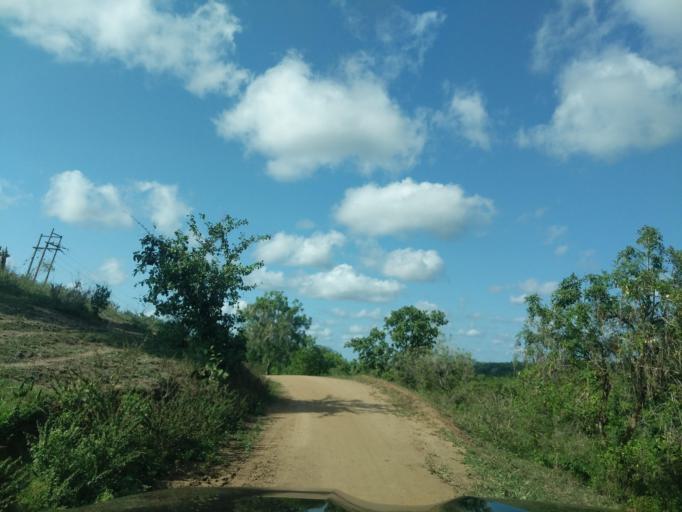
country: TZ
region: Tanga
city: Muheza
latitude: -5.4191
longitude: 38.6475
